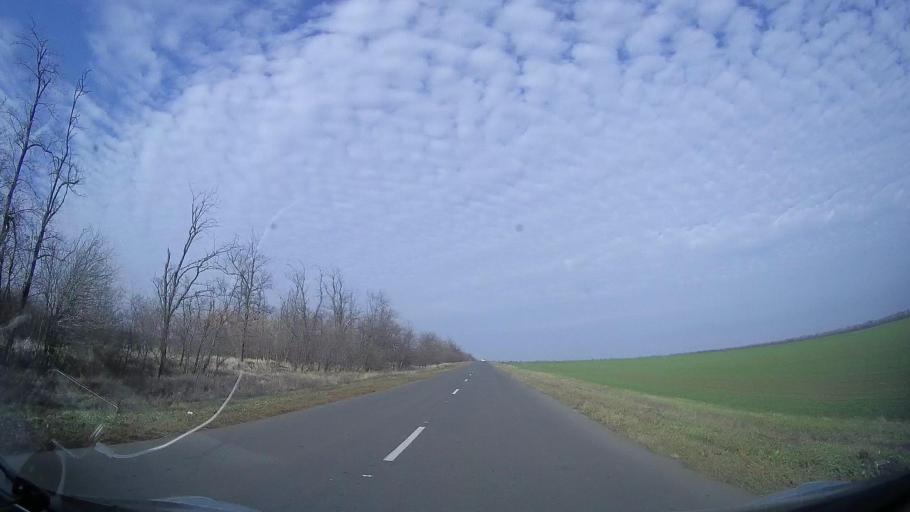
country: RU
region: Rostov
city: Gigant
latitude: 46.8497
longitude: 41.2852
